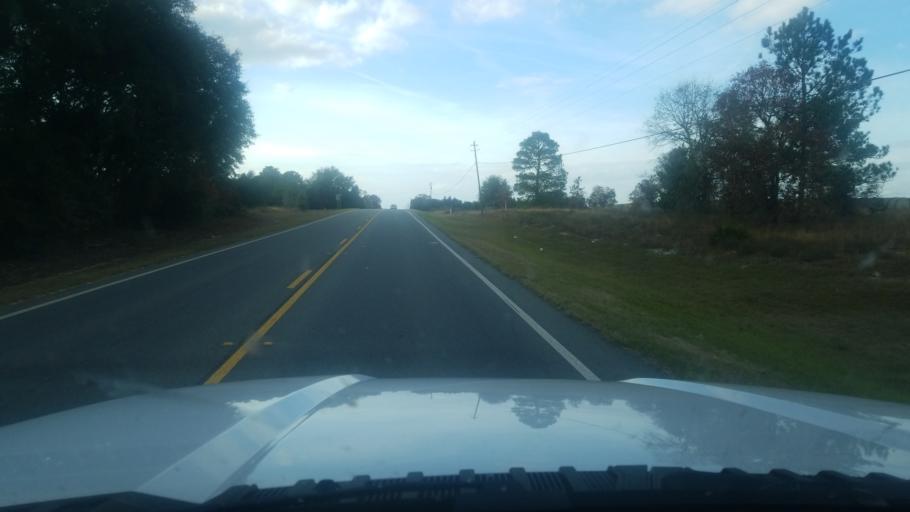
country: US
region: Georgia
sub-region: Tattnall County
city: Reidsville
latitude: 32.0953
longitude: -82.1548
